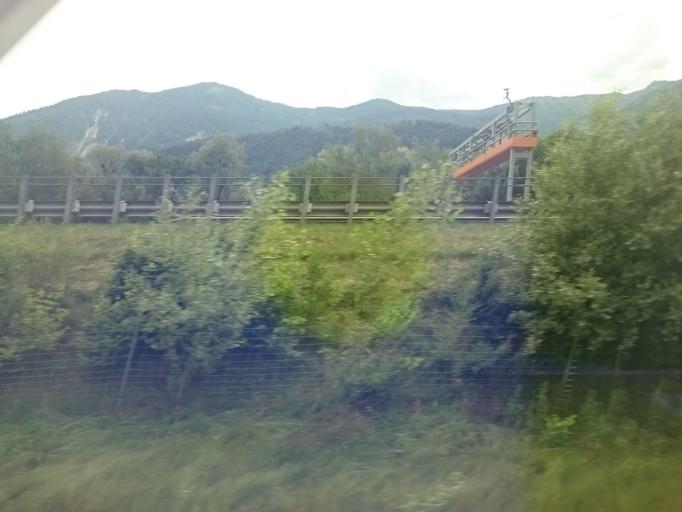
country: AT
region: Tyrol
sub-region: Politischer Bezirk Schwaz
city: Buch bei Jenbach
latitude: 47.3814
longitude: 11.7535
